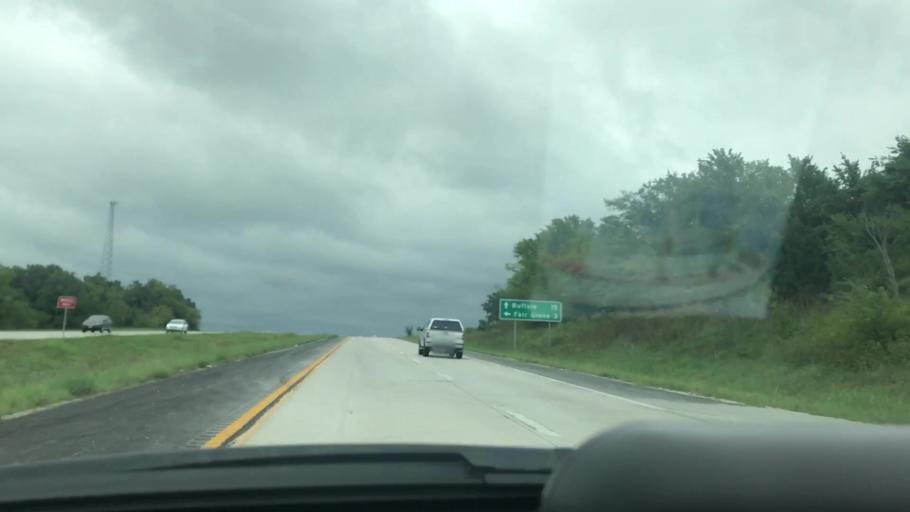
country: US
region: Missouri
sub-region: Greene County
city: Fair Grove
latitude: 37.4227
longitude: -93.1450
